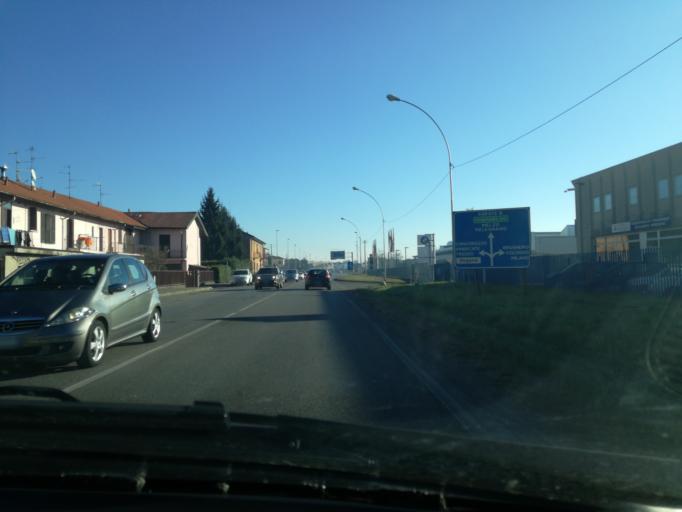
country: IT
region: Lombardy
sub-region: Provincia di Monza e Brianza
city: Concorezzo
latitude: 45.5803
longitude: 9.3194
